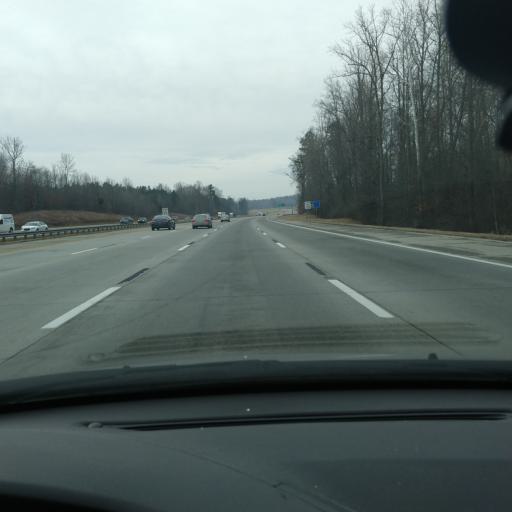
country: US
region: North Carolina
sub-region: Rowan County
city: East Spencer
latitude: 35.6849
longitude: -80.4063
